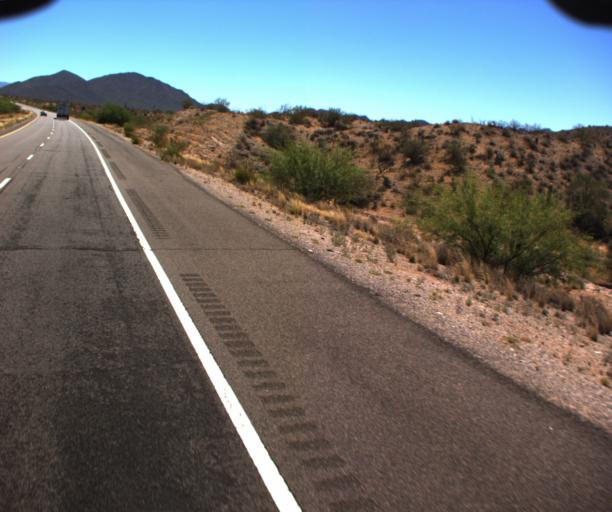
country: US
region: Arizona
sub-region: Maricopa County
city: Fountain Hills
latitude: 33.5810
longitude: -111.6224
